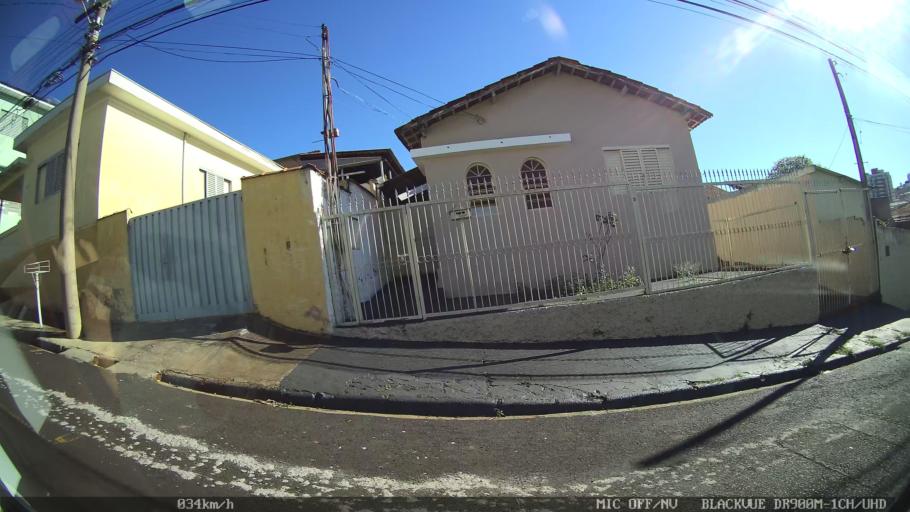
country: BR
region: Sao Paulo
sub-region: Franca
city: Franca
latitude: -20.5415
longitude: -47.4090
